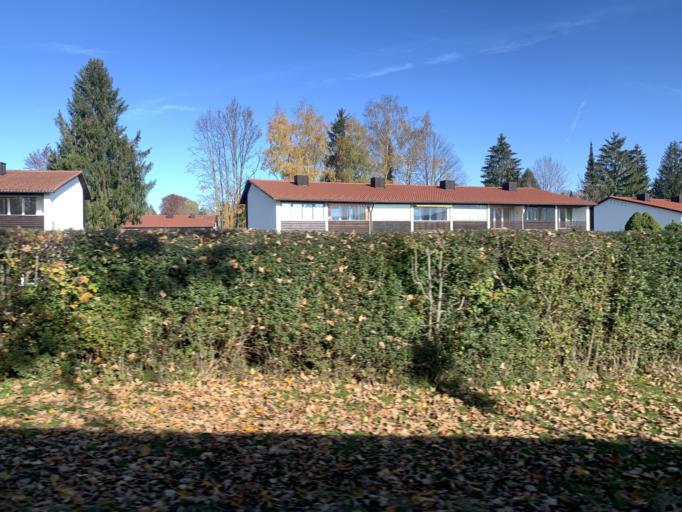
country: DE
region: Bavaria
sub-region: Upper Bavaria
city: Gmund am Tegernsee
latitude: 47.7483
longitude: 11.7283
